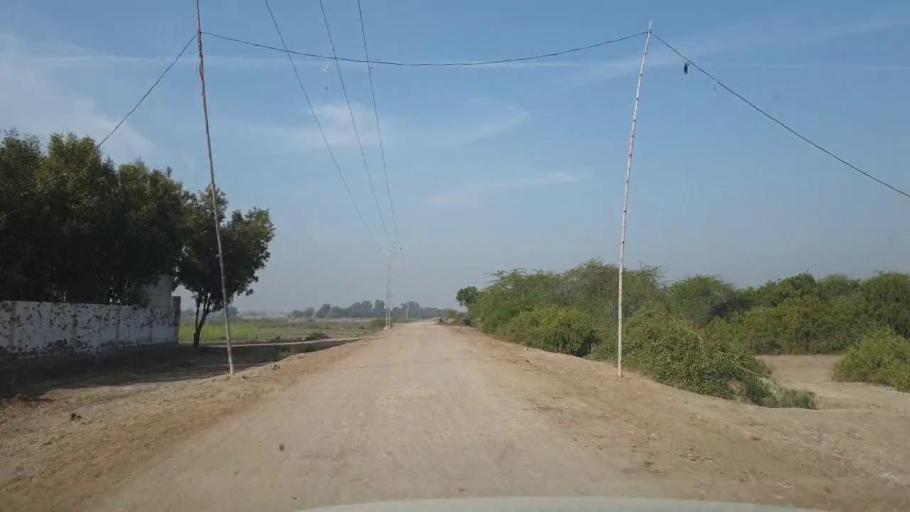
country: PK
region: Sindh
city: Mirpur Khas
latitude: 25.5093
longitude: 69.0414
